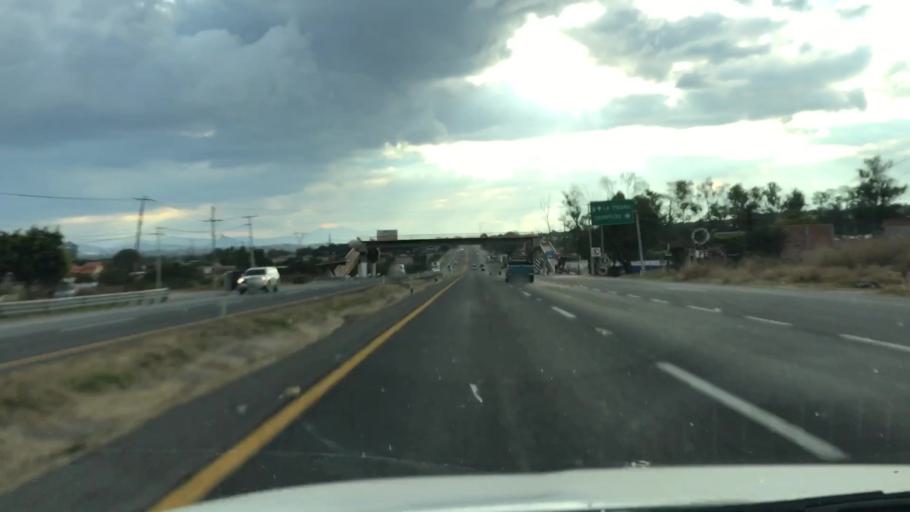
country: MX
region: Guanajuato
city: Penjamo
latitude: 20.4097
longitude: -101.7375
